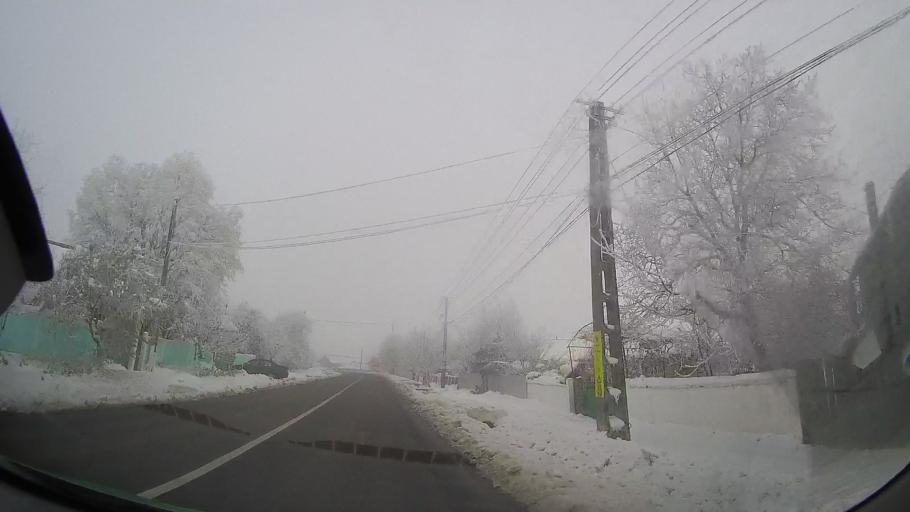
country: RO
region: Iasi
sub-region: Comuna Mircesti
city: Mircesti
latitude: 47.0945
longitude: 26.8196
